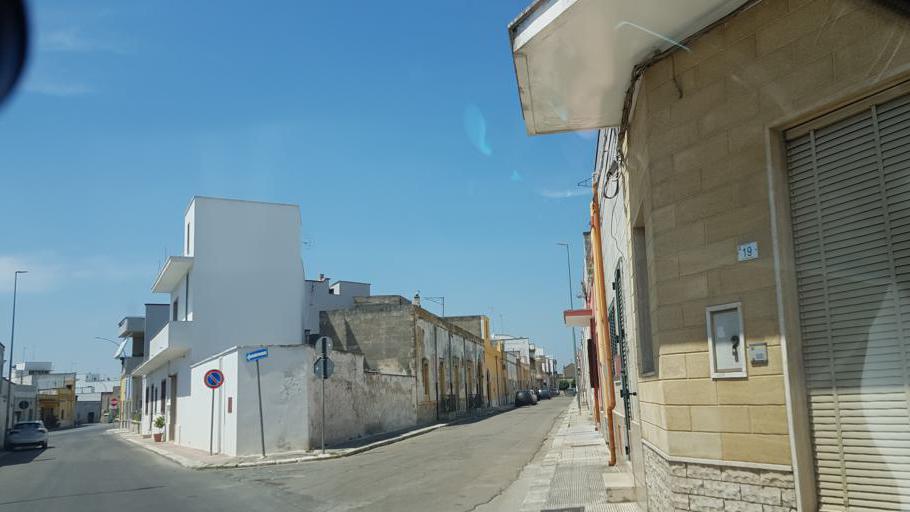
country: IT
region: Apulia
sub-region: Provincia di Brindisi
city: San Donaci
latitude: 40.4457
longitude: 17.9250
